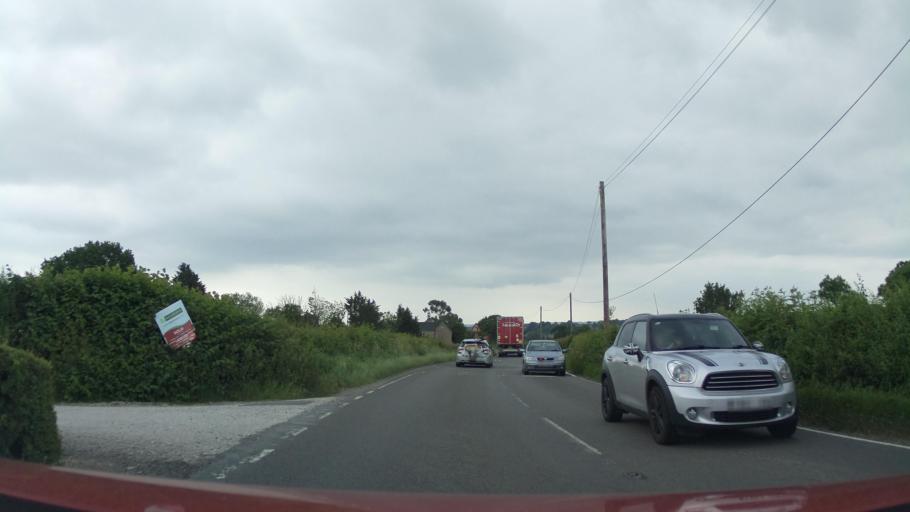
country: GB
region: England
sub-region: Staffordshire
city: Mayfield
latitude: 52.9516
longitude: -1.7578
